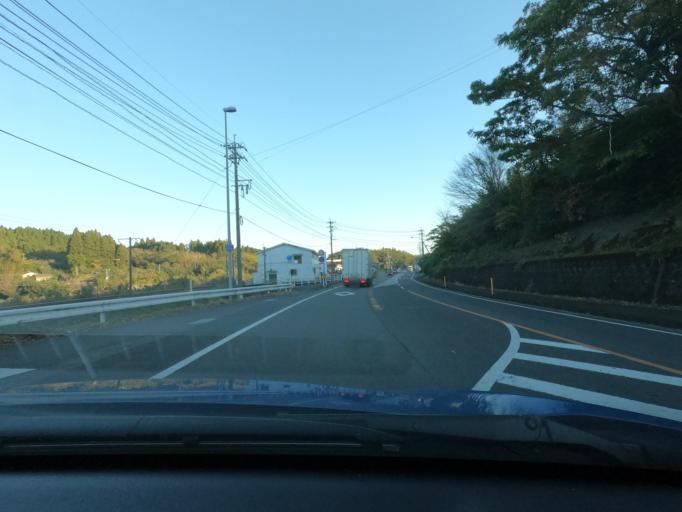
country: JP
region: Kagoshima
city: Satsumasendai
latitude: 31.8434
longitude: 130.2797
